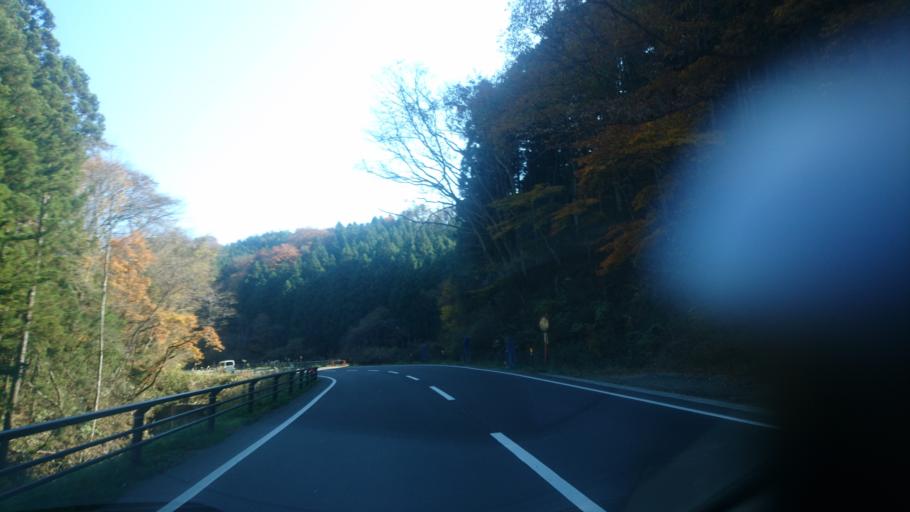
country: JP
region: Miyagi
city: Okawara
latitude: 38.1307
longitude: 140.7596
